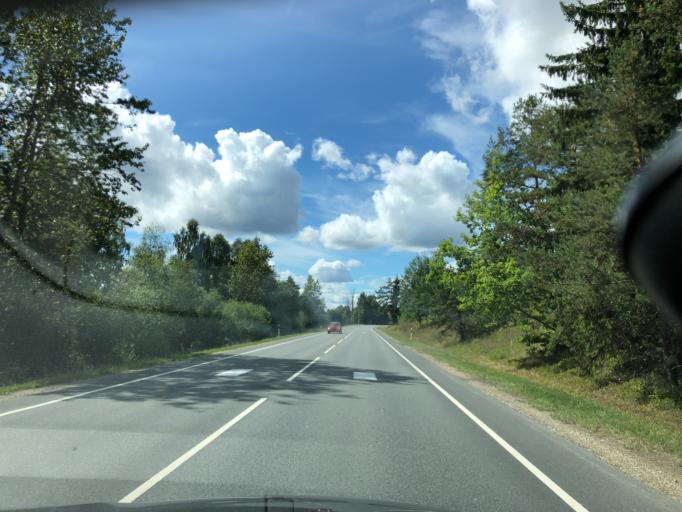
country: EE
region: Harju
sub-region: Nissi vald
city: Turba
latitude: 59.0022
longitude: 24.1138
